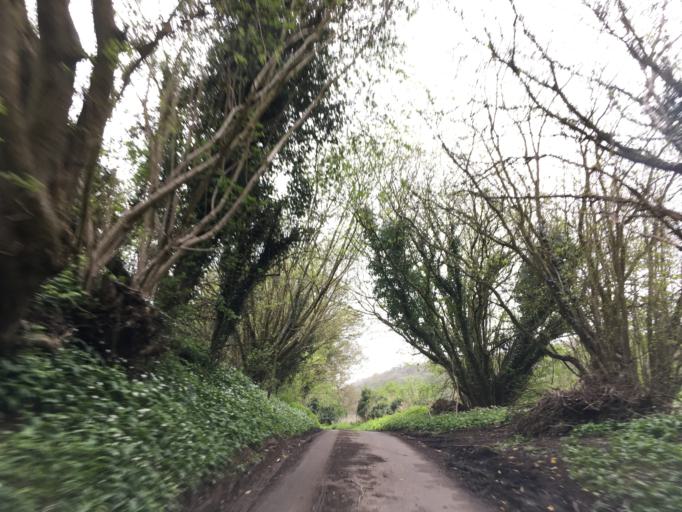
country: GB
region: England
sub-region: Gloucestershire
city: Wotton-under-Edge
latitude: 51.6298
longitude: -2.3090
